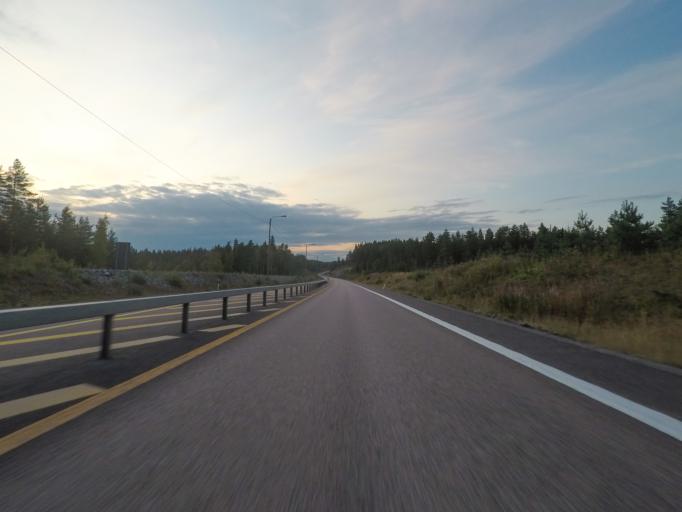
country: FI
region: Central Finland
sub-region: Jyvaeskylae
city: Saeynaetsalo
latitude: 62.1909
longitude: 25.9012
